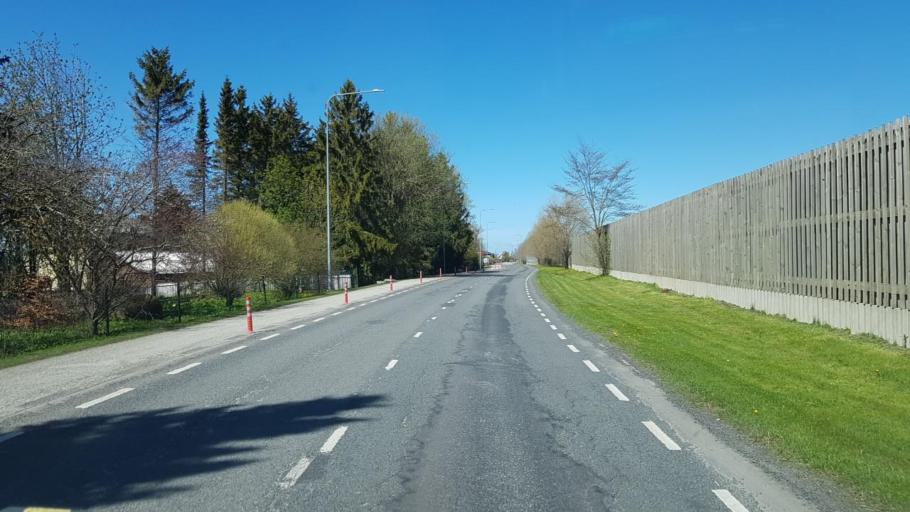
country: EE
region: Harju
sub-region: Viimsi vald
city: Haabneeme
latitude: 59.4999
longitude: 24.8241
